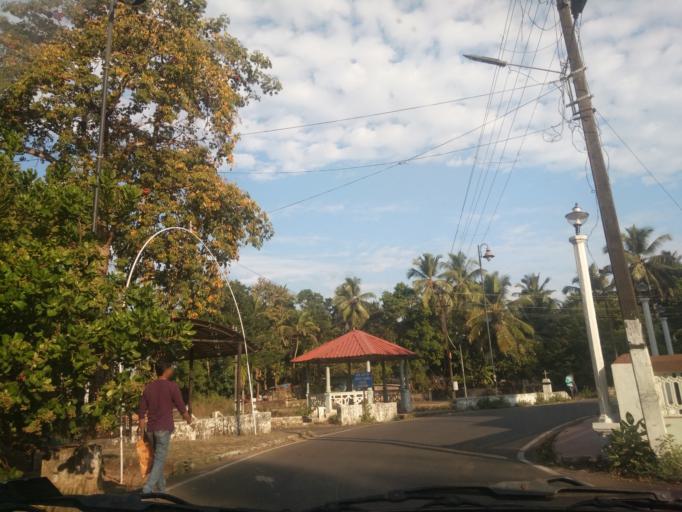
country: IN
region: Goa
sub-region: South Goa
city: Varca
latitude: 15.2431
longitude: 73.9564
